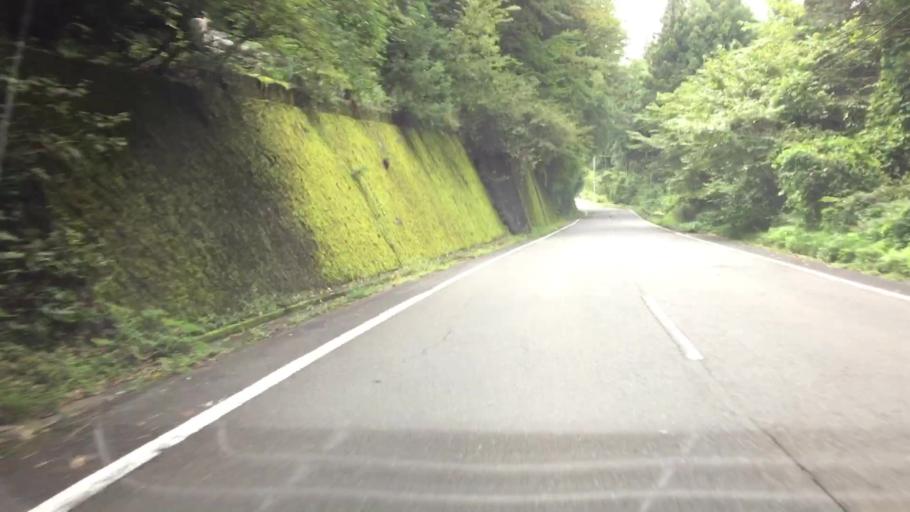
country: JP
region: Tochigi
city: Imaichi
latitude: 36.7508
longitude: 139.6855
